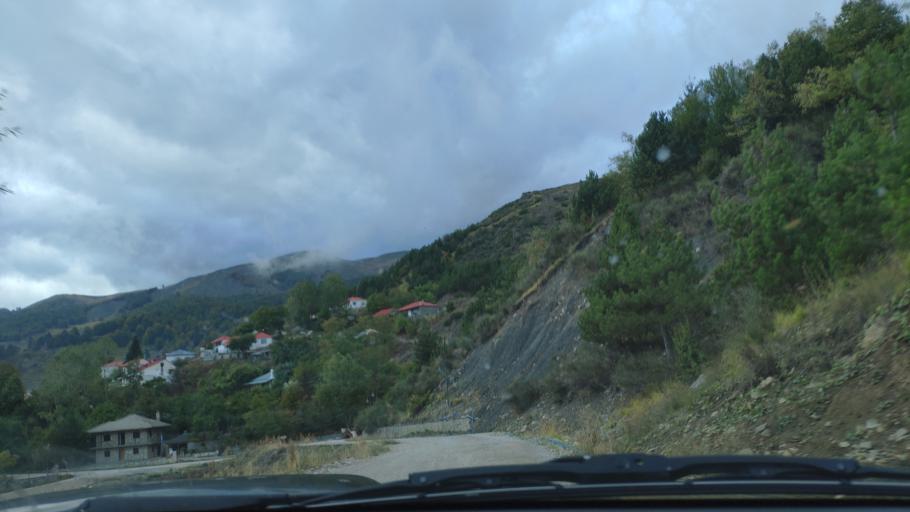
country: AL
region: Korce
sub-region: Rrethi i Kolonjes
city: Erseke
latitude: 40.3110
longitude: 20.8592
